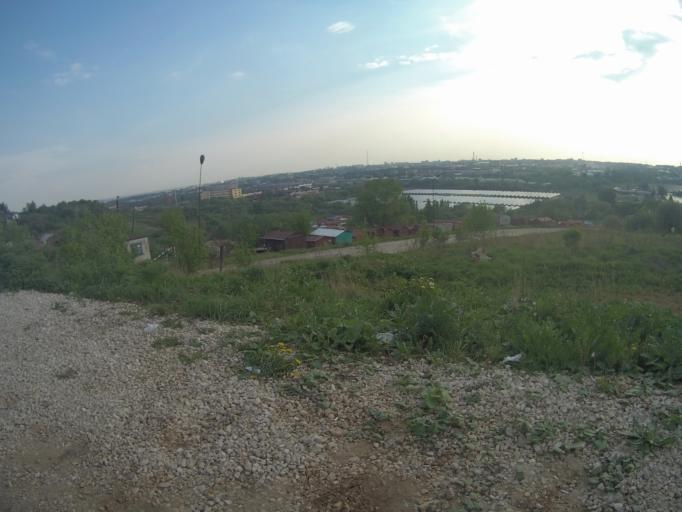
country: RU
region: Vladimir
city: Vladimir
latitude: 56.1666
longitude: 40.4397
